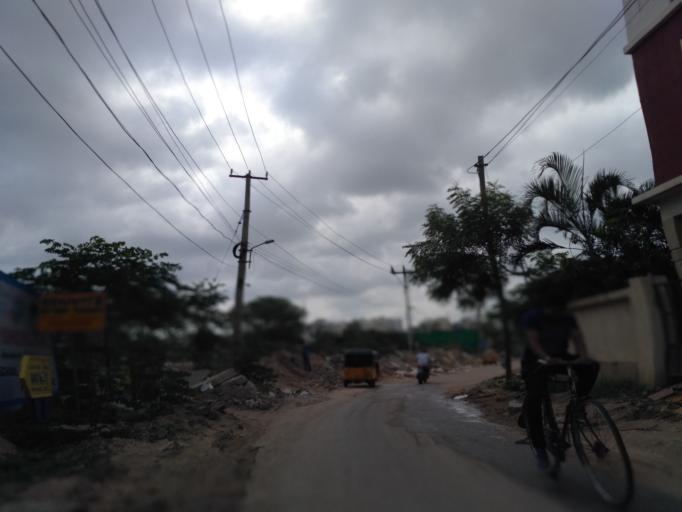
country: IN
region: Telangana
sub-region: Rangareddi
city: Kukatpalli
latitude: 17.4470
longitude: 78.3938
